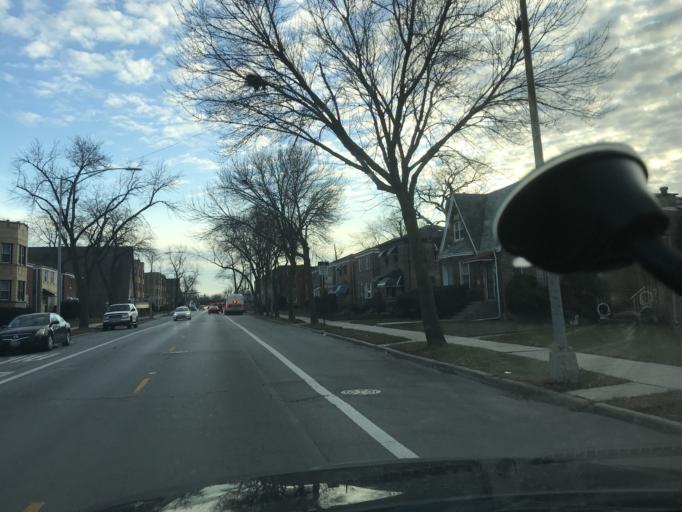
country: US
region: Indiana
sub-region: Lake County
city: Whiting
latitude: 41.7471
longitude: -87.5759
